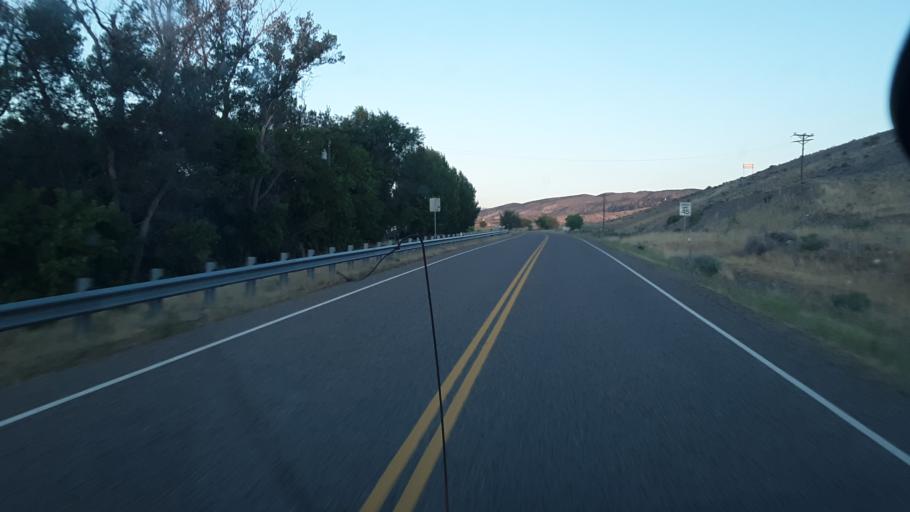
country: US
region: Utah
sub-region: Sevier County
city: Monroe
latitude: 38.6032
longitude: -112.2365
